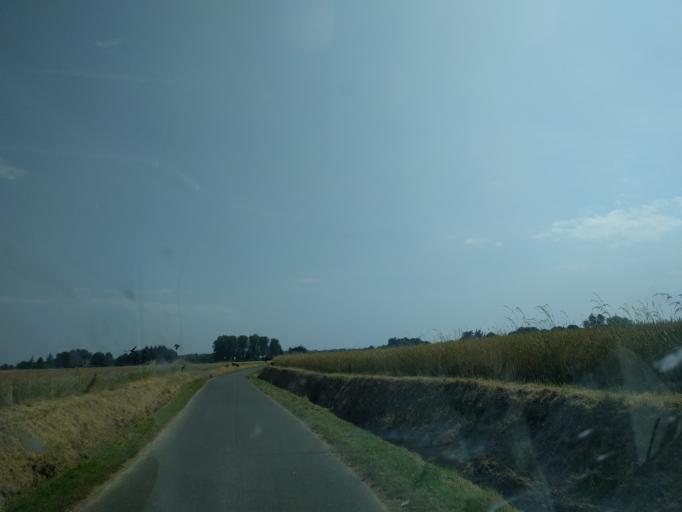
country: FR
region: Brittany
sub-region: Departement des Cotes-d'Armor
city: Erquy
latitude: 48.5731
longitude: -2.4620
